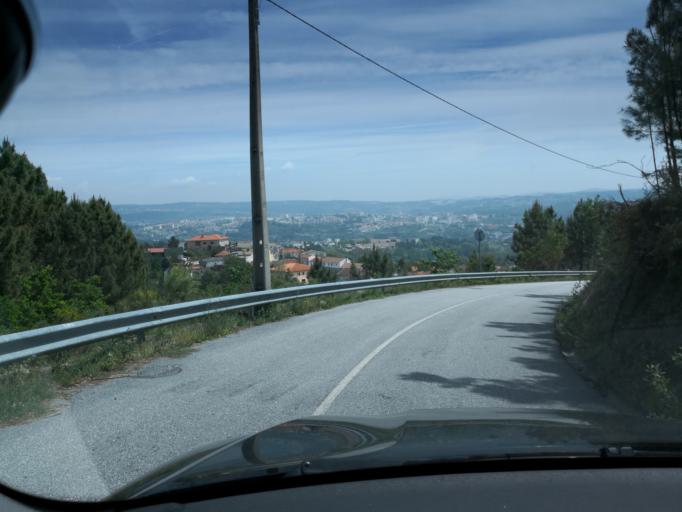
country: PT
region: Vila Real
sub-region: Vila Real
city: Vila Real
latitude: 41.3110
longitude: -7.7818
